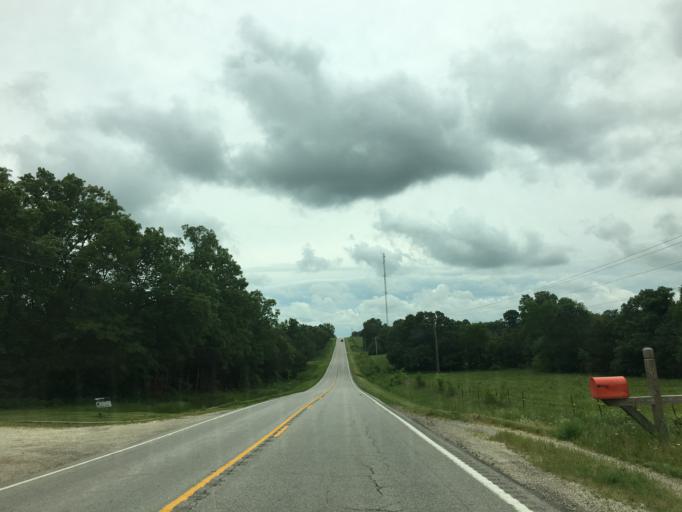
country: US
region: Missouri
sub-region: Gasconade County
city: Owensville
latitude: 38.4955
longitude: -91.4620
